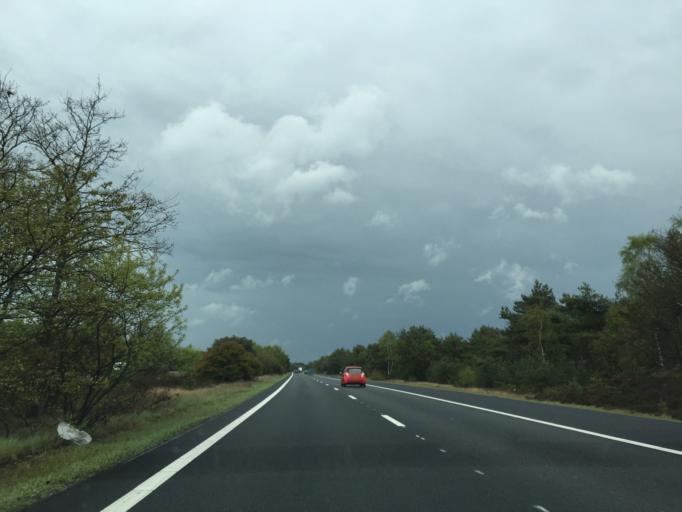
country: NL
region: Gelderland
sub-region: Gemeente Oldebroek
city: Oldebroek
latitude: 52.4158
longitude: 5.9052
